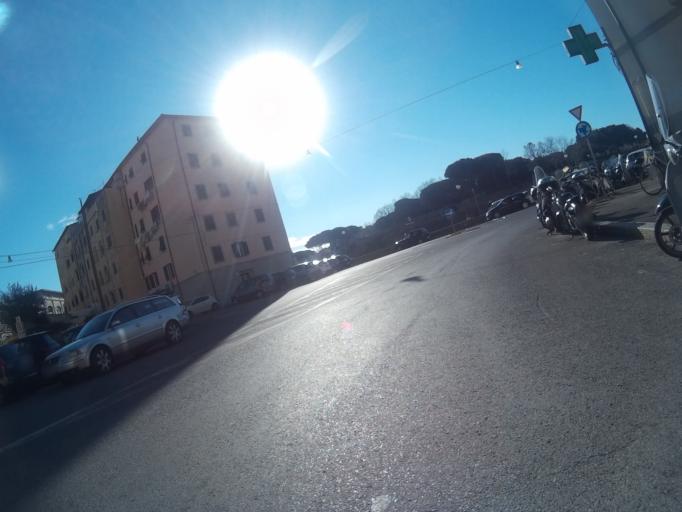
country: IT
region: Tuscany
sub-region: Provincia di Livorno
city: Livorno
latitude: 43.5565
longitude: 10.3126
